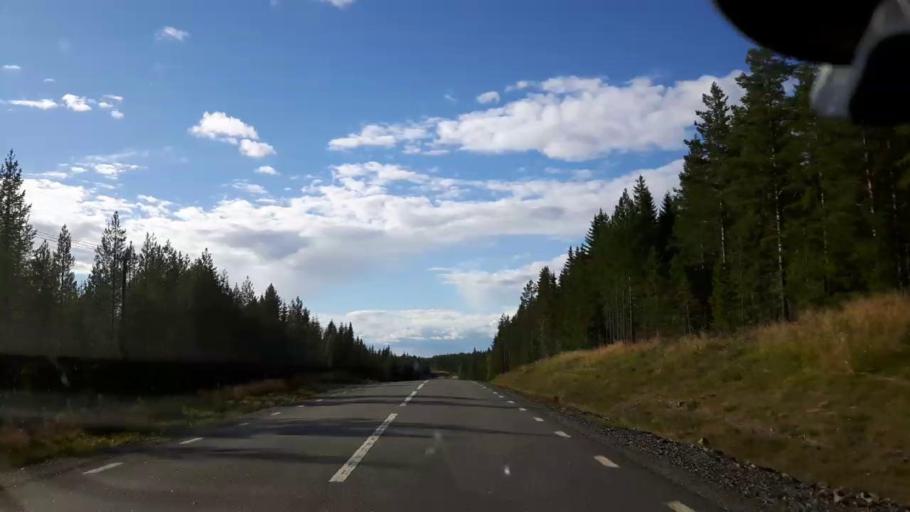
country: SE
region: Jaemtland
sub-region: Stroemsunds Kommun
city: Stroemsund
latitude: 63.5440
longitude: 15.9131
